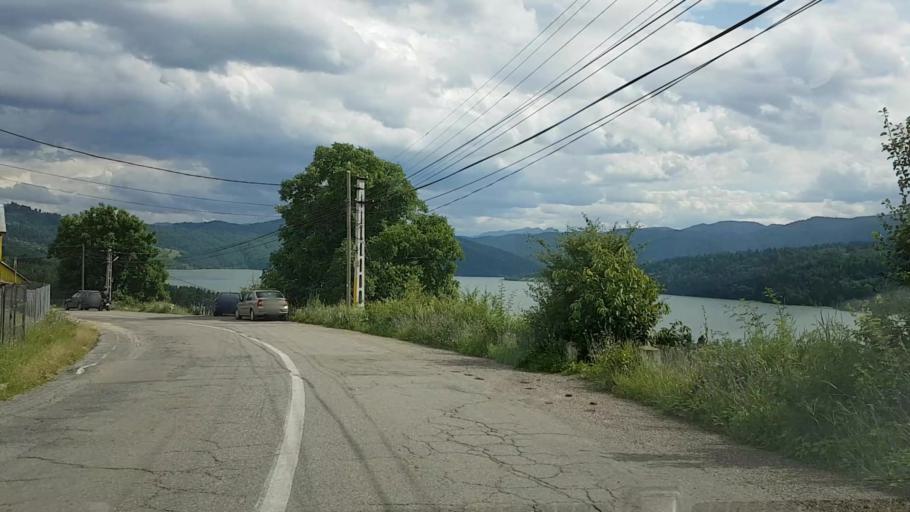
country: RO
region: Neamt
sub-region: Comuna Hangu
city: Hangu
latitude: 47.0186
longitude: 26.0731
